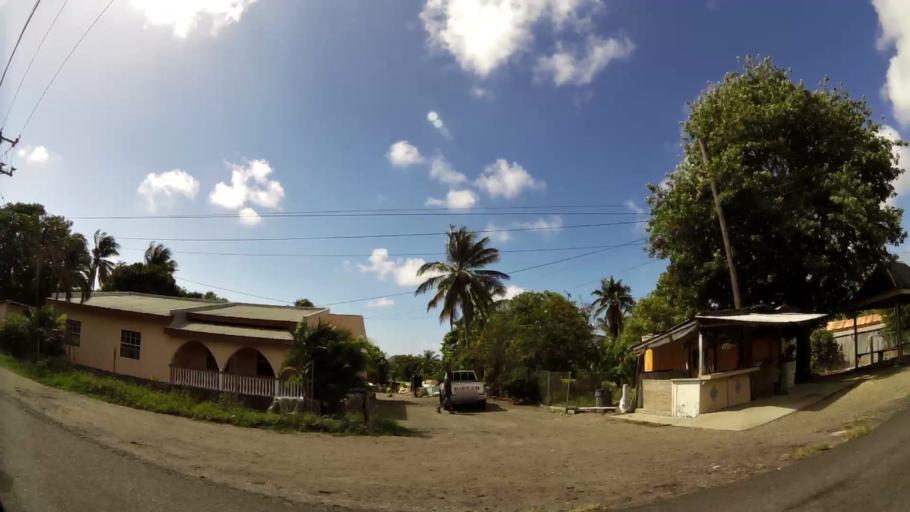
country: LC
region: Laborie Quarter
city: Laborie
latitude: 13.7590
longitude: -60.9738
